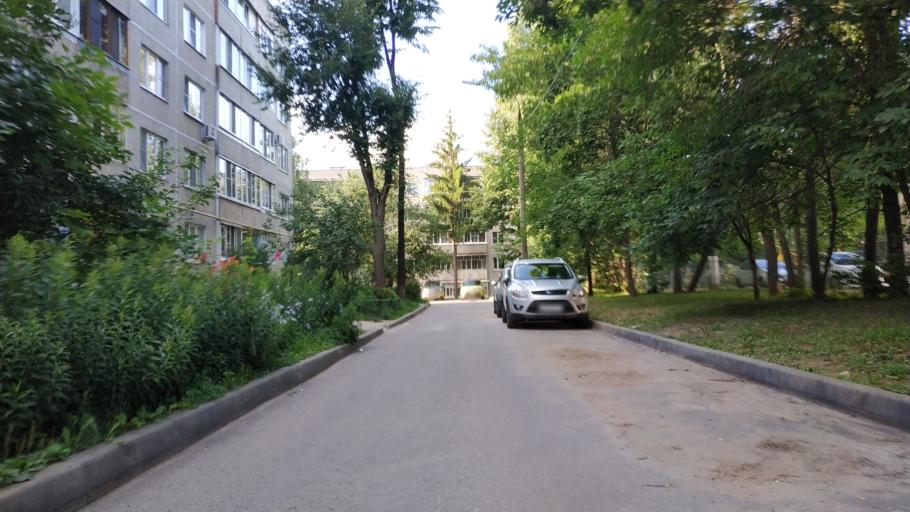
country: RU
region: Chuvashia
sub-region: Cheboksarskiy Rayon
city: Cheboksary
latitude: 56.1447
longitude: 47.1826
